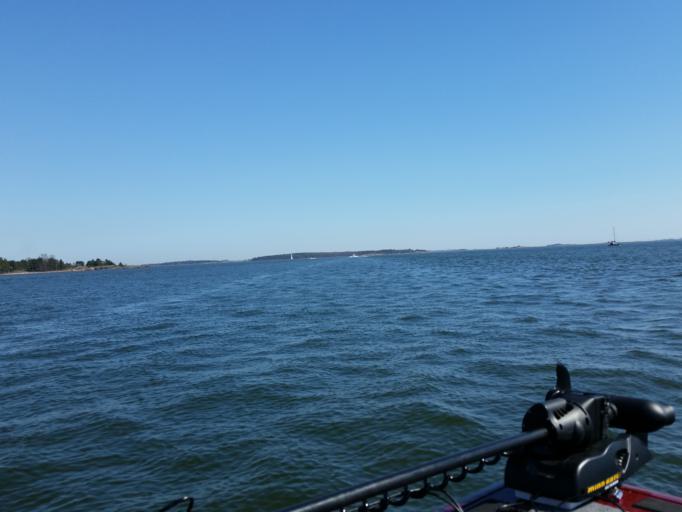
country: FI
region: Uusimaa
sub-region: Helsinki
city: Otaniemi
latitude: 60.1392
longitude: 24.8162
